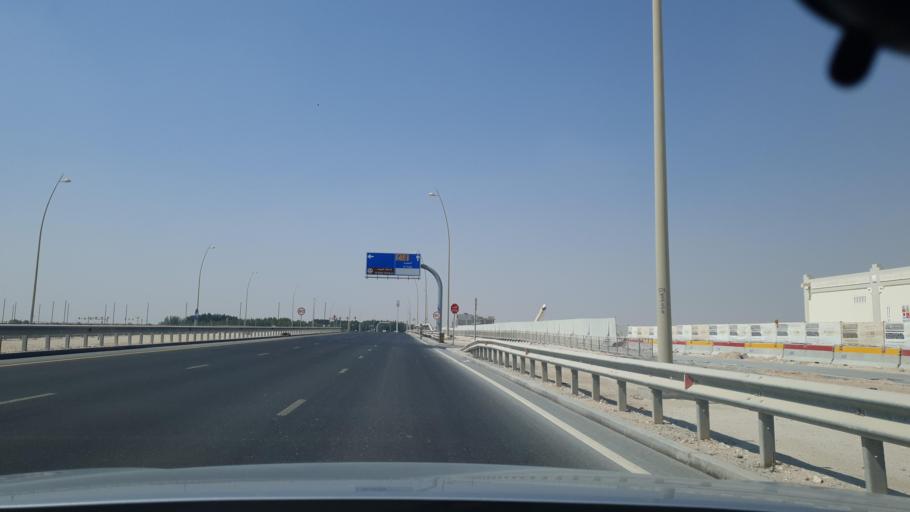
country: QA
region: Al Khawr
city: Al Khawr
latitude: 25.6614
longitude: 51.4882
